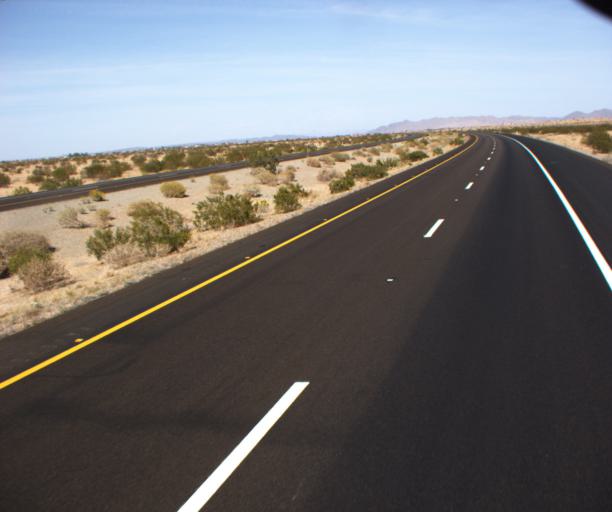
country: US
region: Arizona
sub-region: Yuma County
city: Fortuna Foothills
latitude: 32.6069
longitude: -114.5303
